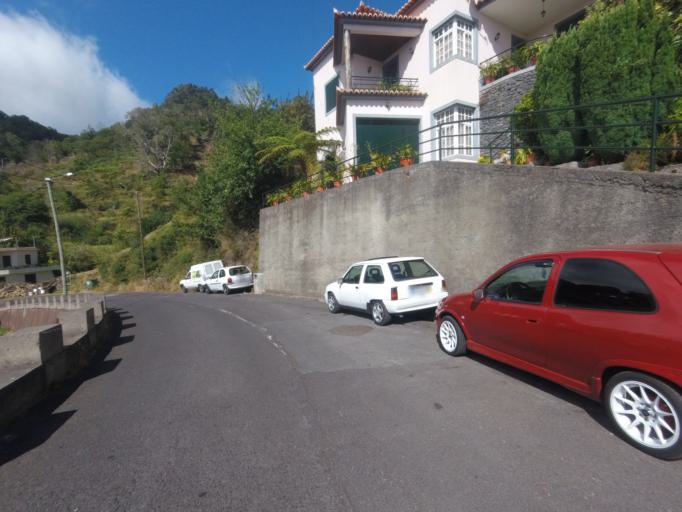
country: PT
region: Madeira
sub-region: Ribeira Brava
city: Campanario
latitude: 32.7028
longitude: -17.0184
